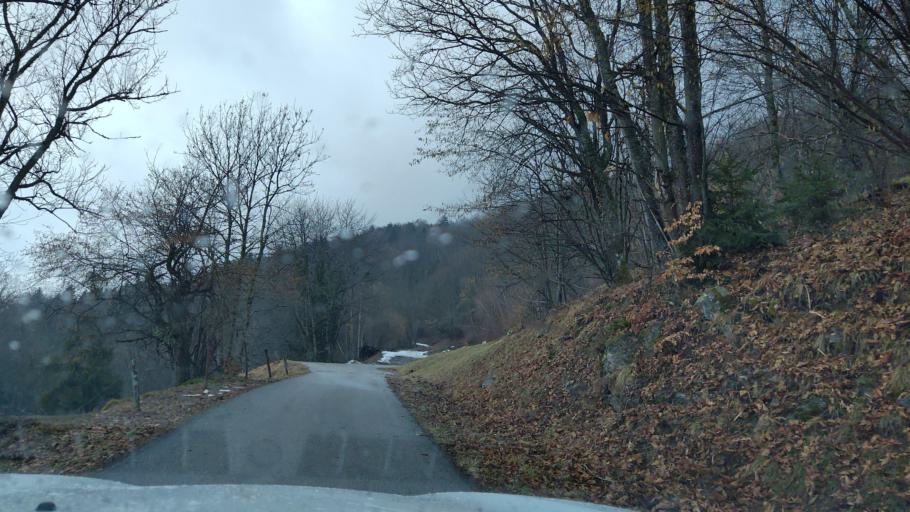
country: FR
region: Rhone-Alpes
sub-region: Departement de la Savoie
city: Aiton
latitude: 45.5086
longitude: 6.2798
